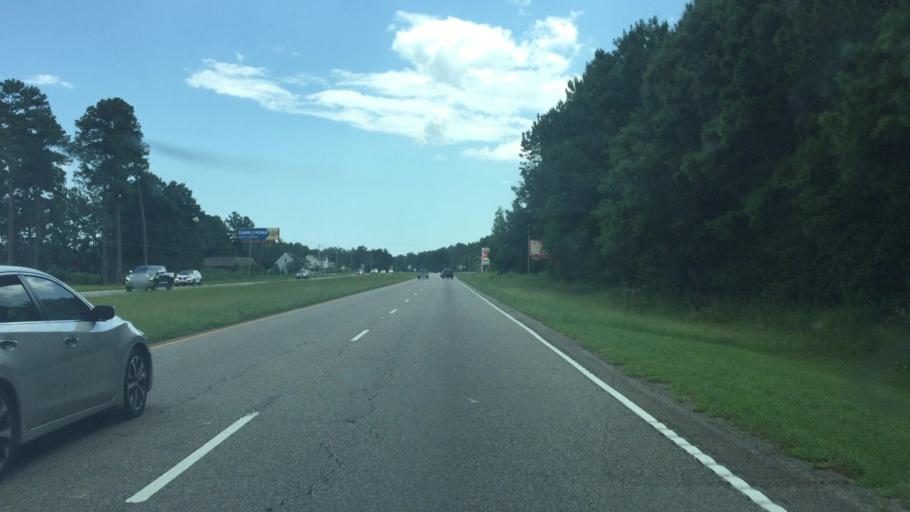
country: US
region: South Carolina
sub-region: Horry County
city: North Myrtle Beach
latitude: 33.9284
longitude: -78.7271
